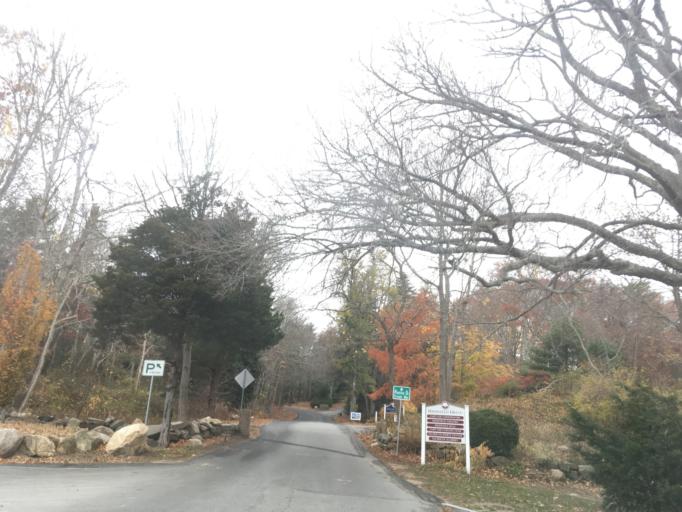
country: US
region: Massachusetts
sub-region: Barnstable County
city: Falmouth
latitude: 41.5566
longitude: -70.6237
